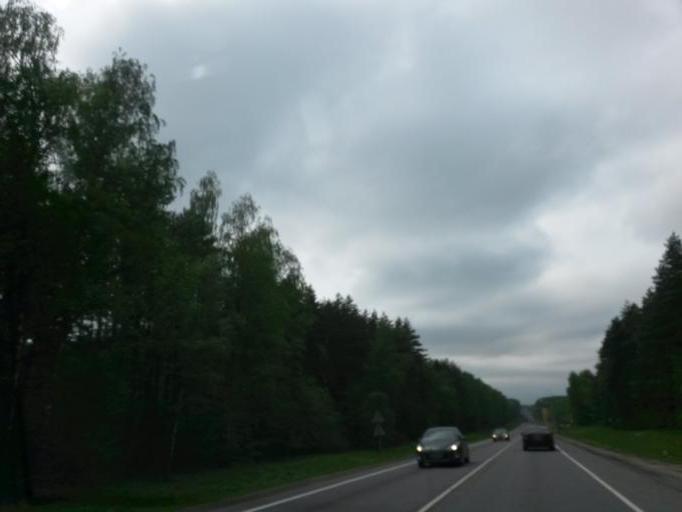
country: RU
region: Moskovskaya
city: Klimovsk
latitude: 55.3314
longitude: 37.6297
